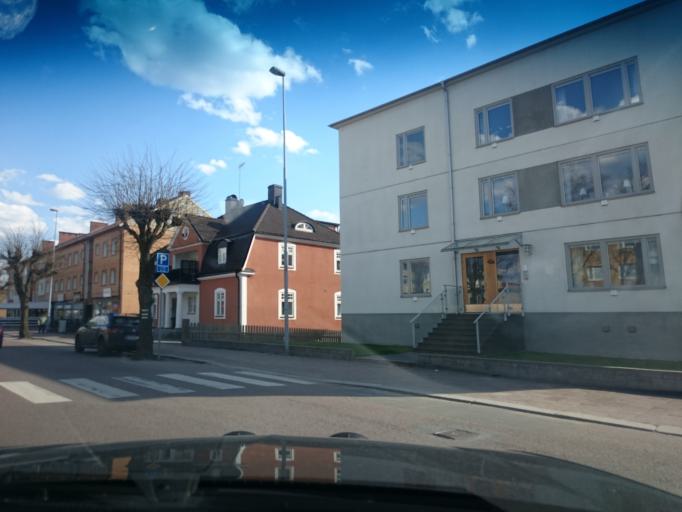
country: SE
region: Joenkoeping
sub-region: Vetlanda Kommun
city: Vetlanda
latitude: 57.4288
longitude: 15.0778
